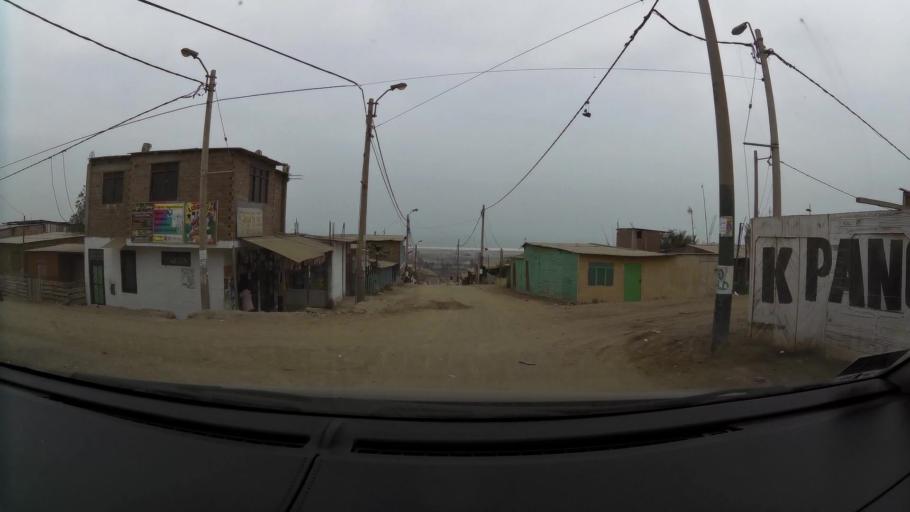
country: PE
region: Lima
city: Ventanilla
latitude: -11.8513
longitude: -77.1507
